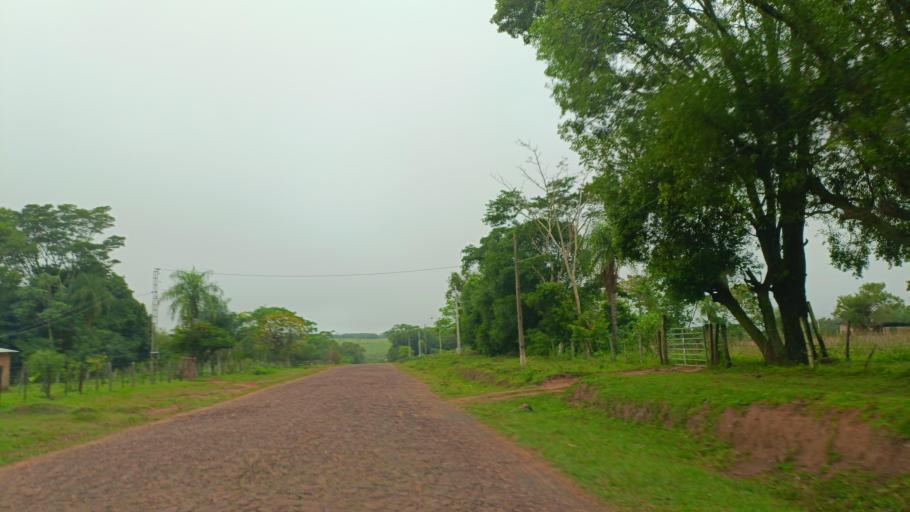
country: PY
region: Misiones
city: Santa Maria
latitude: -26.8627
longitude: -57.0150
